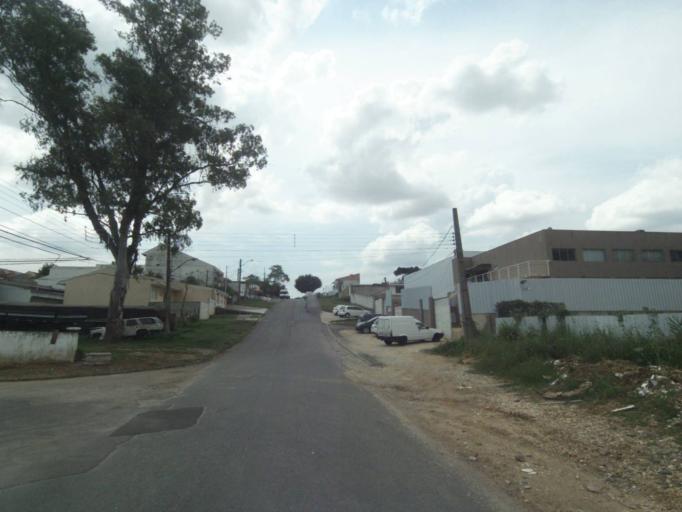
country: BR
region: Parana
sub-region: Pinhais
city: Pinhais
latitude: -25.3956
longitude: -49.1987
